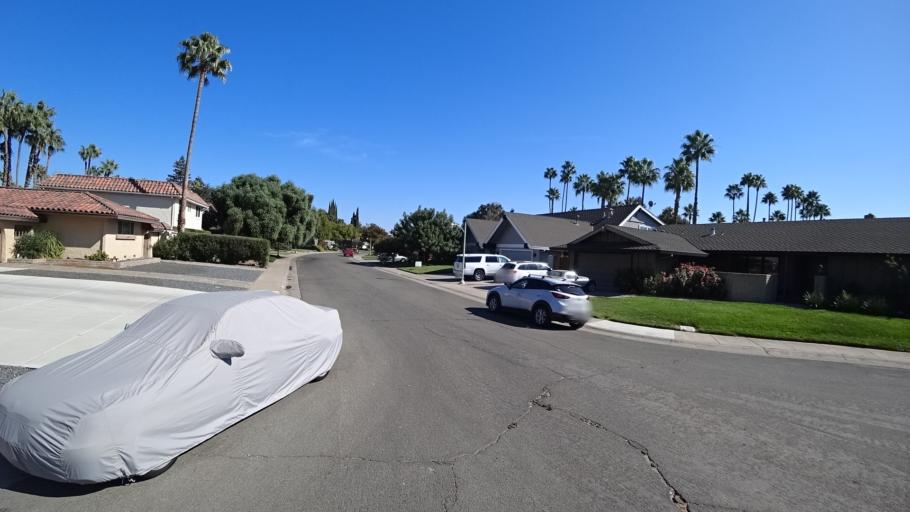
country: US
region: California
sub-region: Yolo County
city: West Sacramento
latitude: 38.5075
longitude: -121.5325
